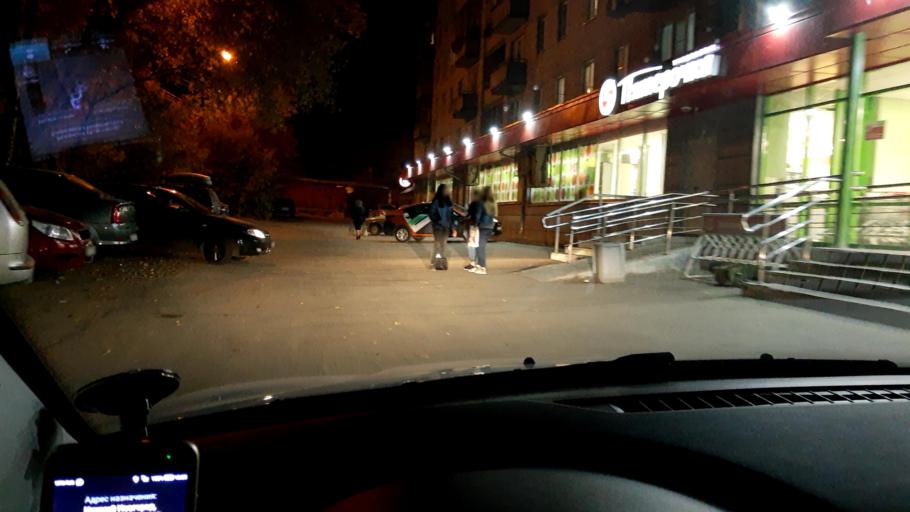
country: RU
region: Nizjnij Novgorod
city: Nizhniy Novgorod
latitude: 56.2974
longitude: 43.9925
